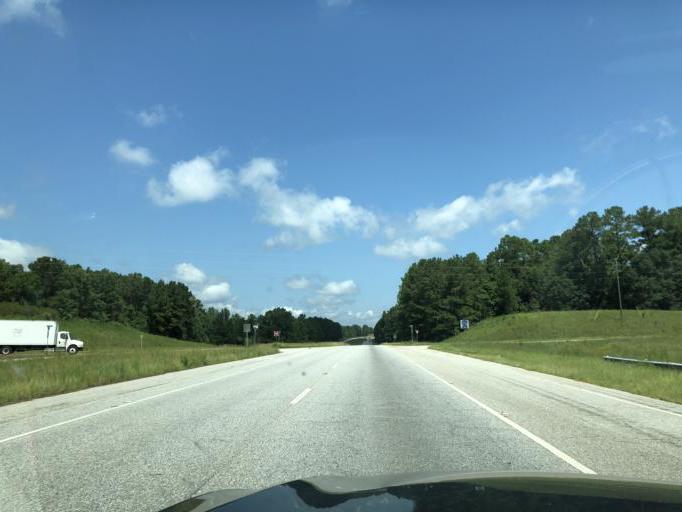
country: US
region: Alabama
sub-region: Henry County
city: Abbeville
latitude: 31.6888
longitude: -85.2788
